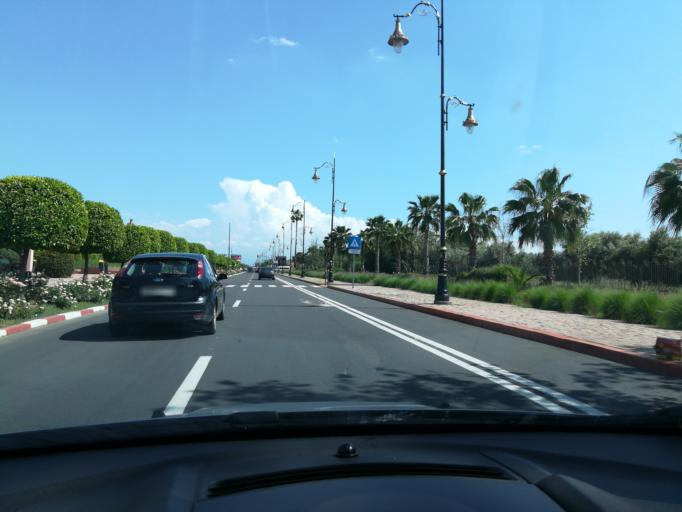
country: MA
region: Marrakech-Tensift-Al Haouz
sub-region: Marrakech
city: Marrakesh
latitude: 31.6117
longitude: -8.0043
